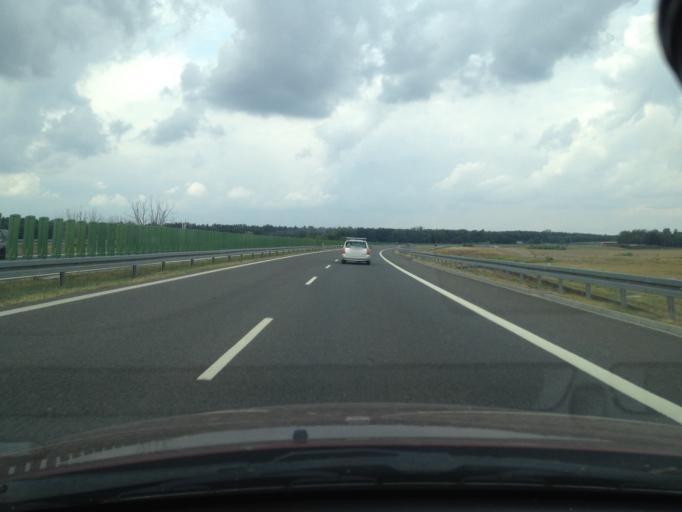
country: PL
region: West Pomeranian Voivodeship
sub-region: Powiat mysliborski
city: Mysliborz
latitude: 52.9862
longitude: 14.8756
